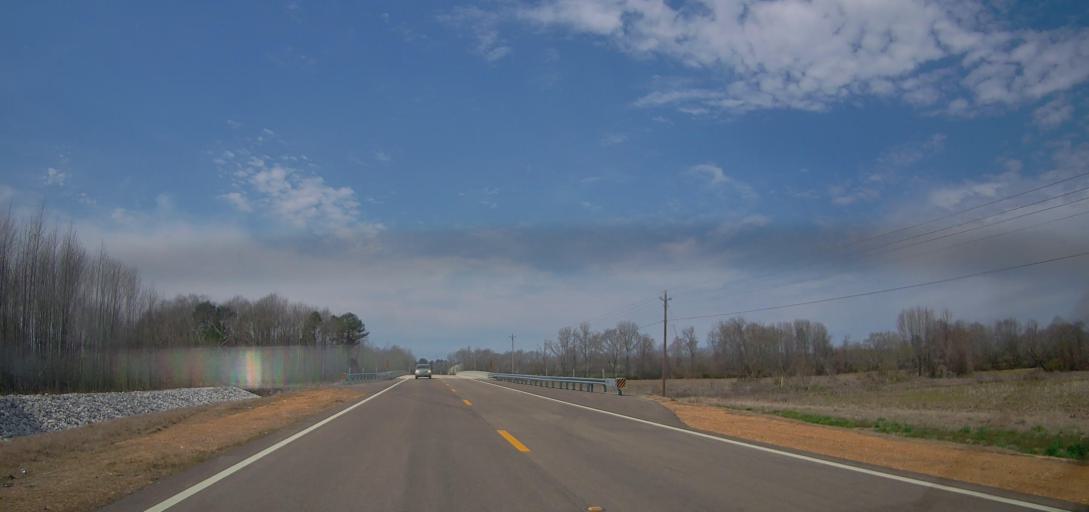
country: US
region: Mississippi
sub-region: Union County
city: New Albany
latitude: 34.6156
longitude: -89.1637
